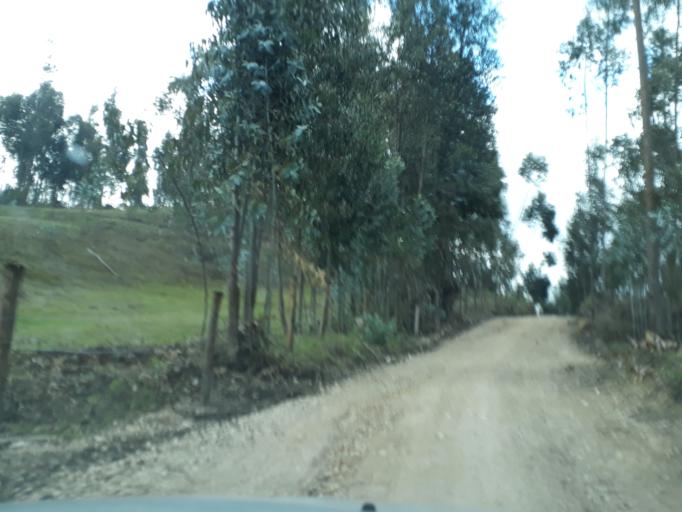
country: CO
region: Cundinamarca
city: Lenguazaque
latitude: 5.2700
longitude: -73.6900
